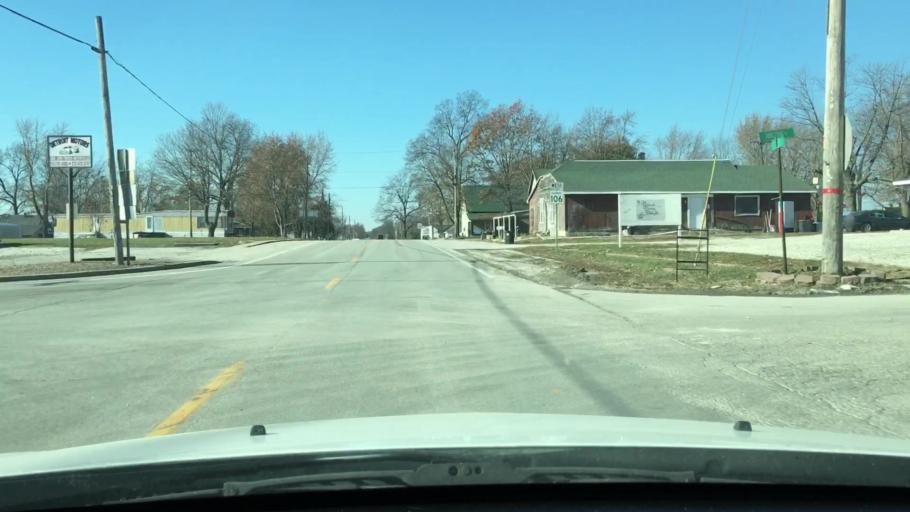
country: US
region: Illinois
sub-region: Pike County
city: Griggsville
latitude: 39.6203
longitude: -90.6758
